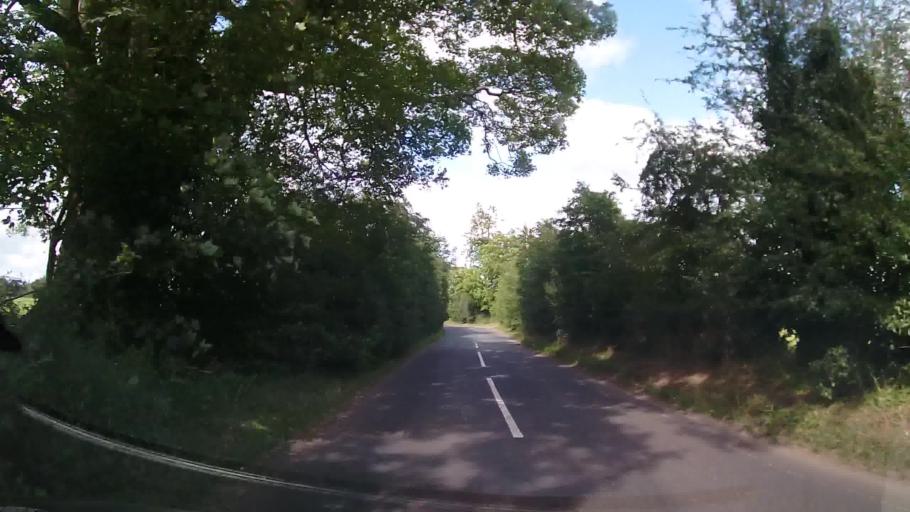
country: GB
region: England
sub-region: Shropshire
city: Petton
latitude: 52.8560
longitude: -2.7913
